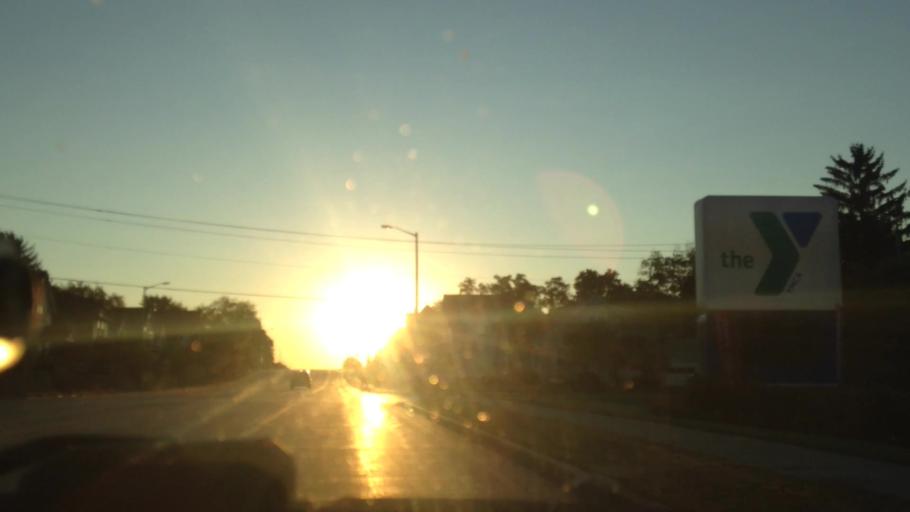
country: US
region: Wisconsin
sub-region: Washington County
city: West Bend
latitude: 43.4268
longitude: -88.1919
